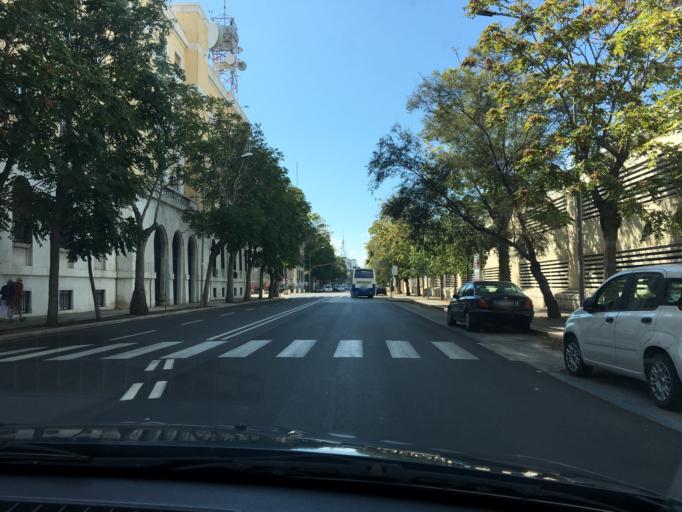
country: IT
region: Apulia
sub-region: Provincia di Bari
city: Bari
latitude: 41.1282
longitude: 16.8596
